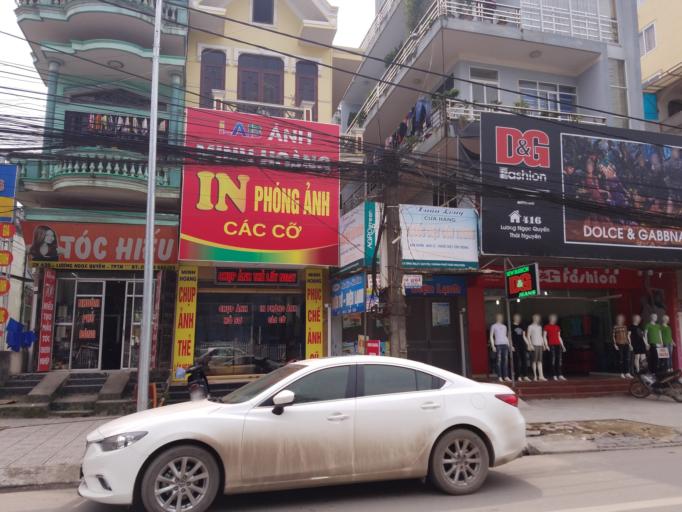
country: VN
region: Thai Nguyen
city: Thanh Pho Thai Nguyen
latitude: 21.5864
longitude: 105.8314
